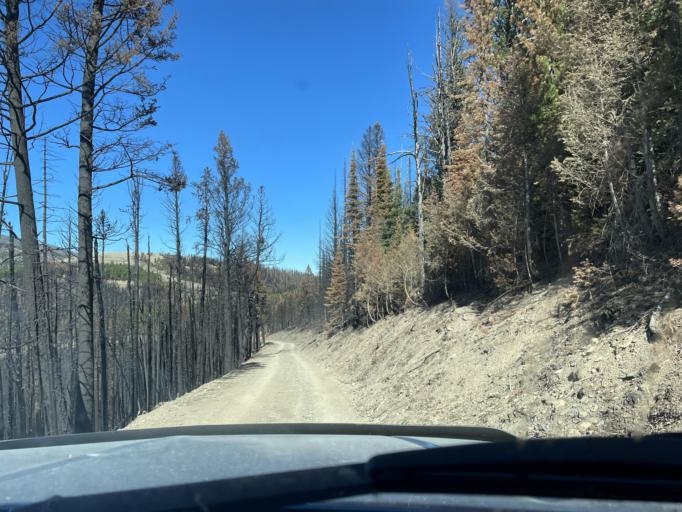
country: US
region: Montana
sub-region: Broadwater County
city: Townsend
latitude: 46.5026
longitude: -111.2757
